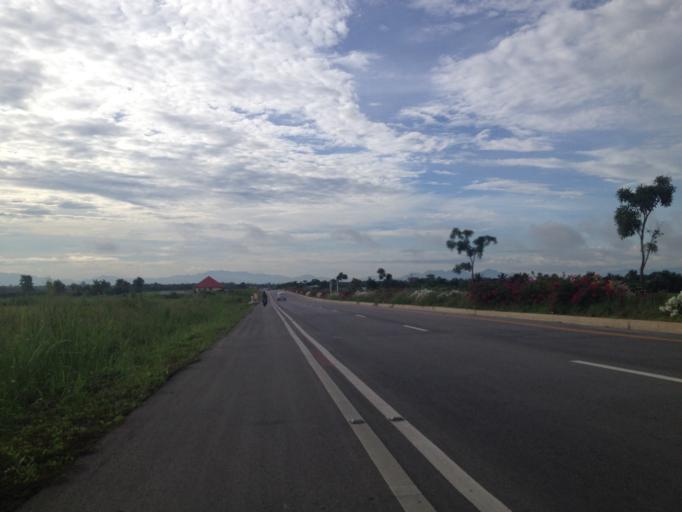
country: TH
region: Chiang Mai
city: San Pa Tong
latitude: 18.5800
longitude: 98.8432
